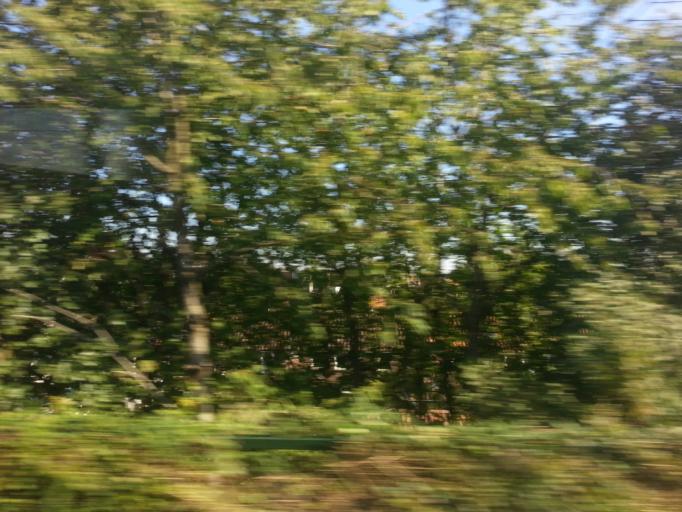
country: NL
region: Utrecht
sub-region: Gemeente Utrecht
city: Utrecht
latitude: 52.1087
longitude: 5.0805
